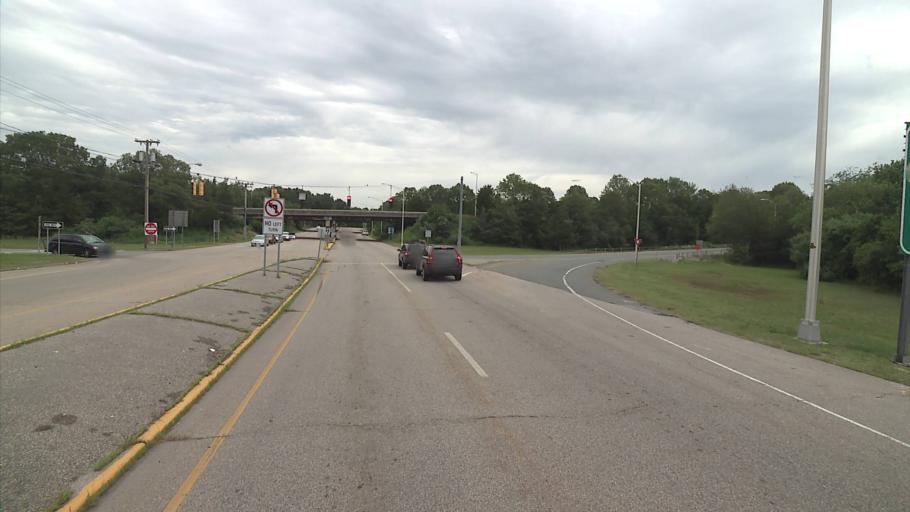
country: US
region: Connecticut
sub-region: New London County
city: Poquonock Bridge
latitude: 41.3603
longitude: -72.0278
